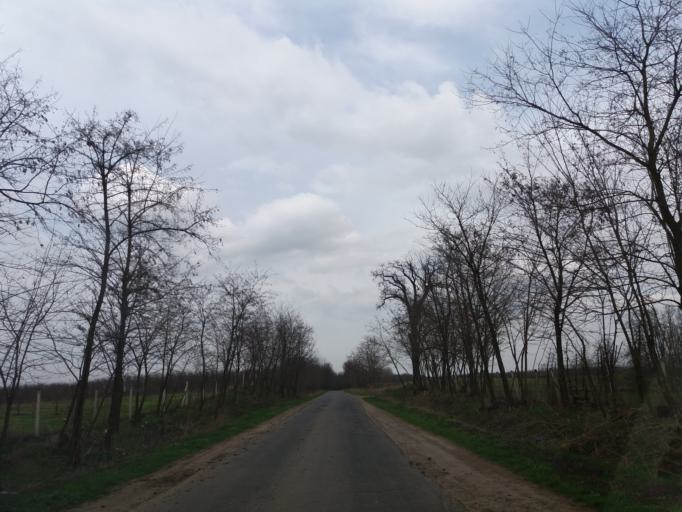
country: HU
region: Szabolcs-Szatmar-Bereg
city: Nyirtass
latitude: 48.1166
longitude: 22.0501
